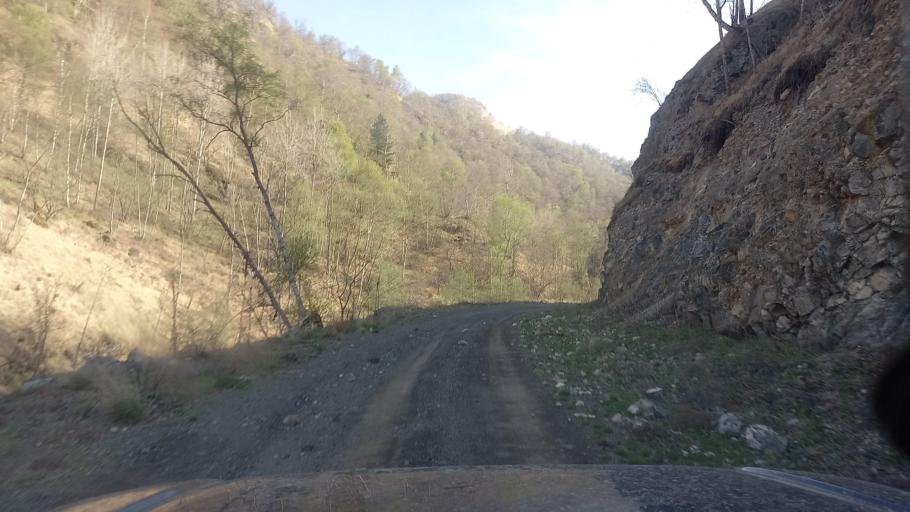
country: RU
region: Kabardino-Balkariya
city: Kamennomostskoye
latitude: 43.7078
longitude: 42.8461
